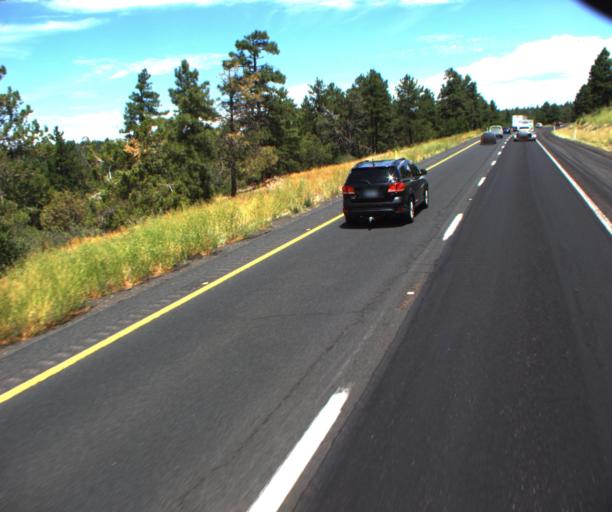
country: US
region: Arizona
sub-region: Yavapai County
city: Village of Oak Creek (Big Park)
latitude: 34.8181
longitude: -111.6117
